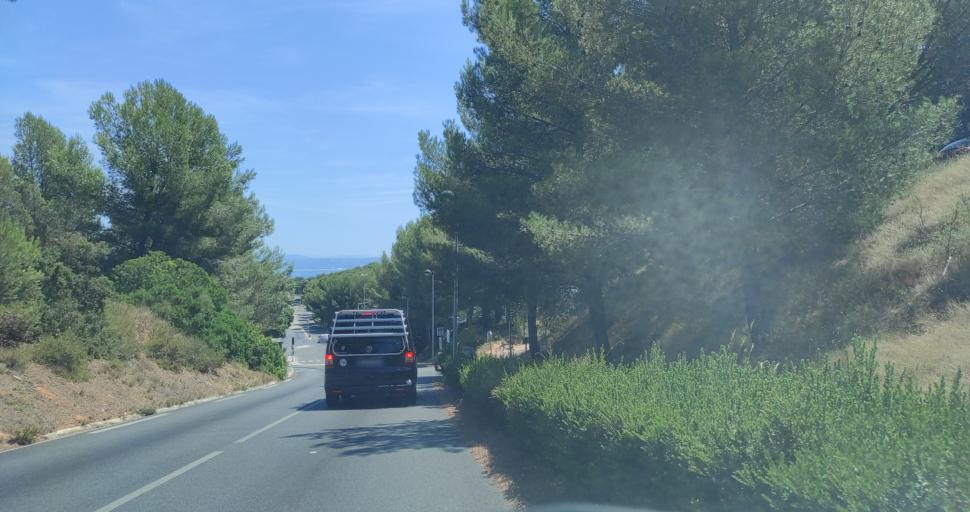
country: FR
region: Provence-Alpes-Cote d'Azur
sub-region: Departement des Bouches-du-Rhone
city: Martigues
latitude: 43.4222
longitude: 5.0491
